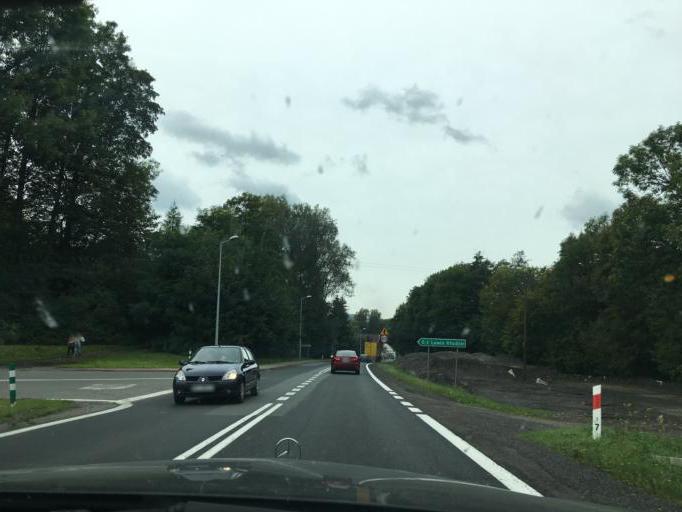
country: PL
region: Lower Silesian Voivodeship
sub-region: Powiat klodzki
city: Lewin Klodzki
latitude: 50.4071
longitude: 16.2814
